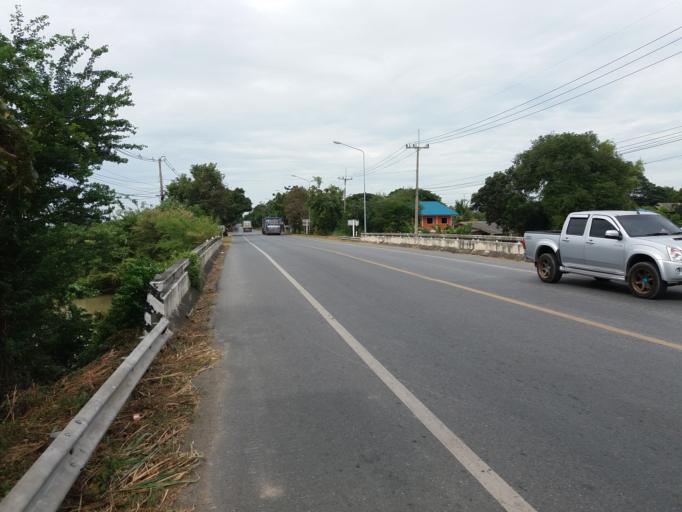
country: TH
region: Sing Buri
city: Bang Racham
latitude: 14.8831
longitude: 100.3504
